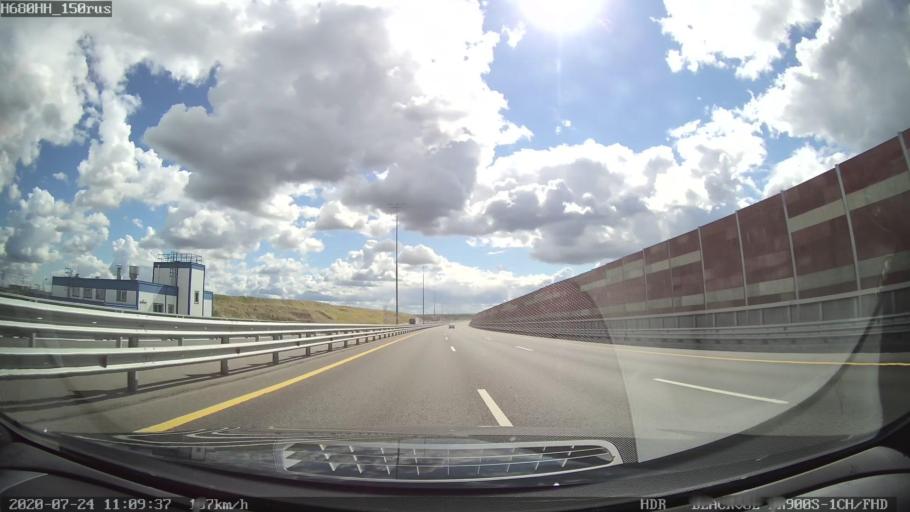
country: RU
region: St.-Petersburg
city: Tyarlevo
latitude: 59.7479
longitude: 30.4798
